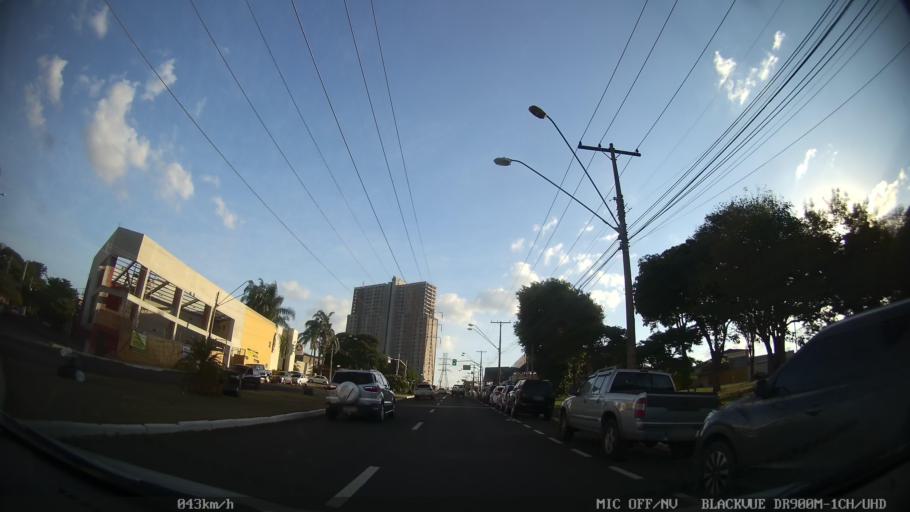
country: BR
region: Sao Paulo
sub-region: Ribeirao Preto
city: Ribeirao Preto
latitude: -21.1954
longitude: -47.8055
